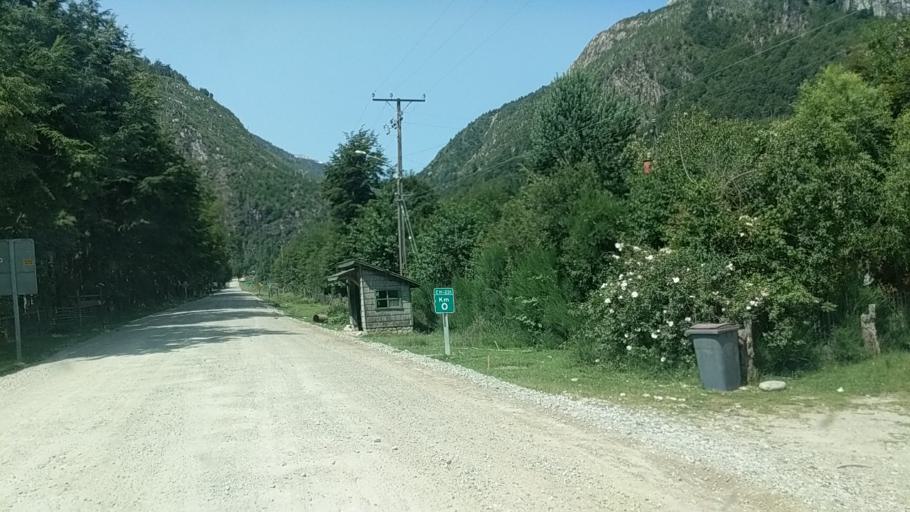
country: CL
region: Los Lagos
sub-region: Provincia de Palena
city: Palena
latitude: -43.4668
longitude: -72.1212
